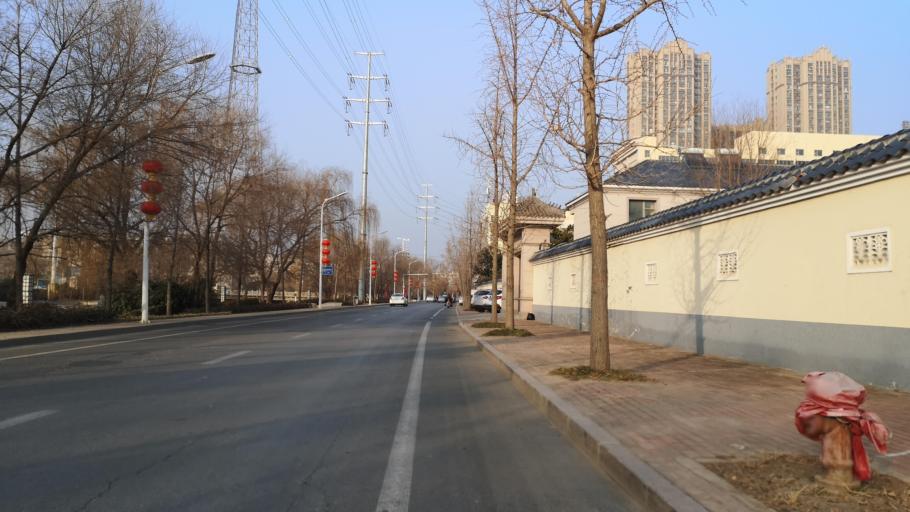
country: CN
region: Henan Sheng
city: Zhongyuanlu
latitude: 35.7781
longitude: 115.0489
